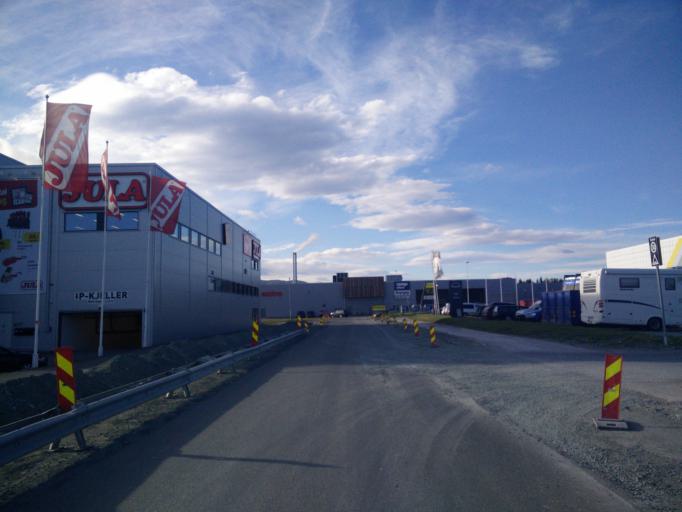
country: NO
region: Sor-Trondelag
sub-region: Trondheim
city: Trondheim
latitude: 63.3556
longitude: 10.3748
